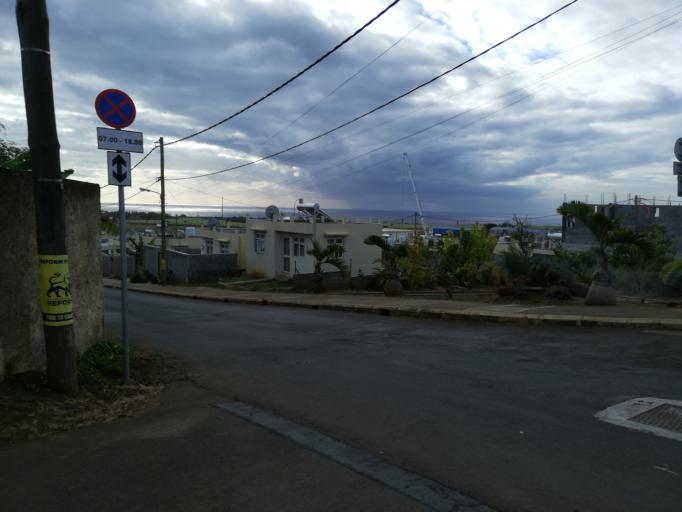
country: MU
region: Black River
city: Petite Riviere
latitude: -20.2211
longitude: 57.4602
